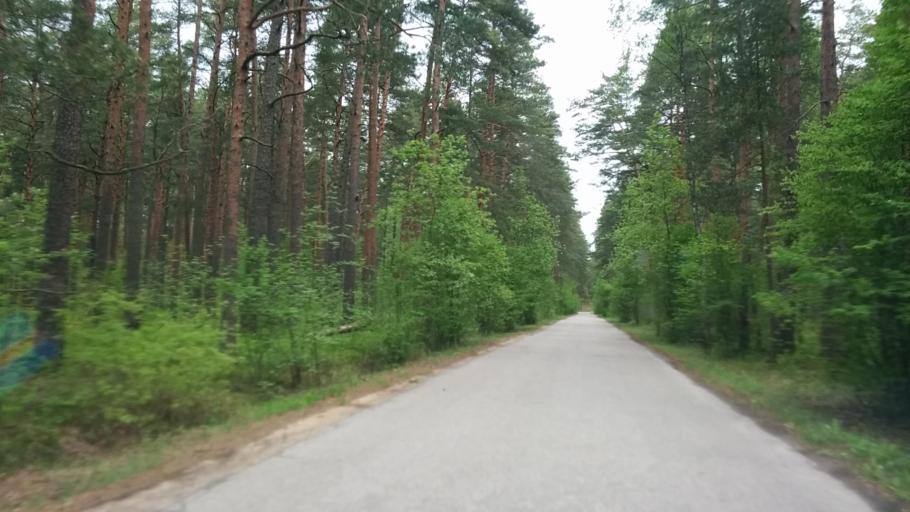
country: LV
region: Babite
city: Pinki
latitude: 56.9376
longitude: 23.9338
